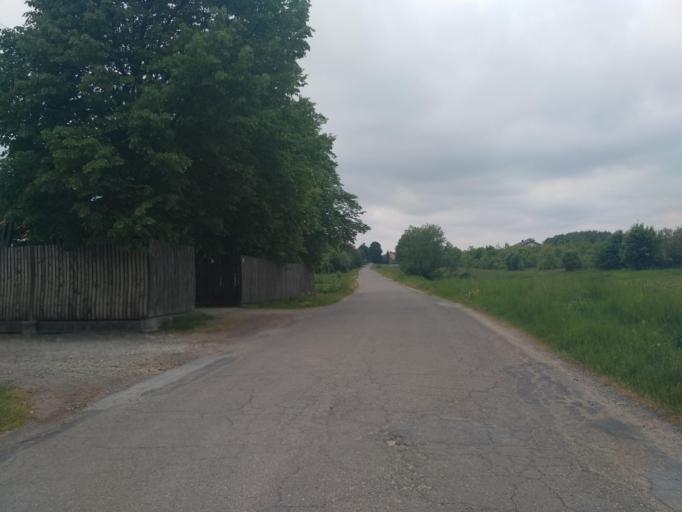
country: PL
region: Subcarpathian Voivodeship
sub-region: Krosno
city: Krosno
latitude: 49.6725
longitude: 21.7417
